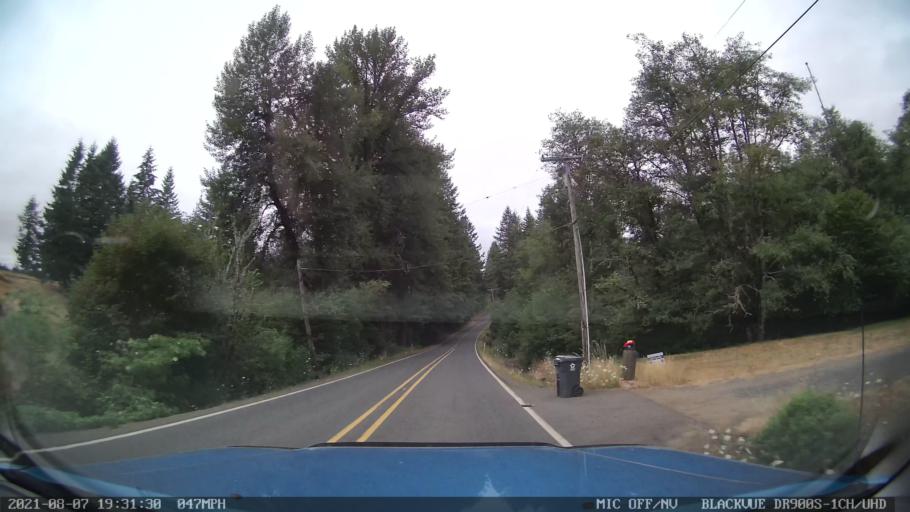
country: US
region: Oregon
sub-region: Linn County
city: Lyons
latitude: 44.8920
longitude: -122.6342
